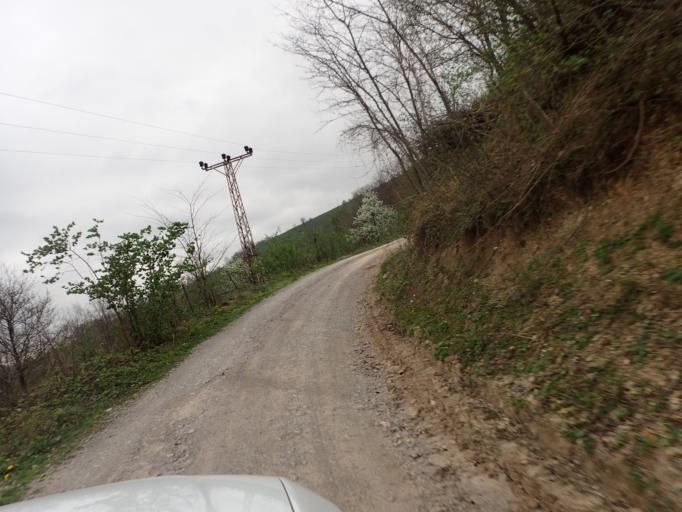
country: TR
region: Ordu
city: Korgan
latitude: 40.7706
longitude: 37.3388
